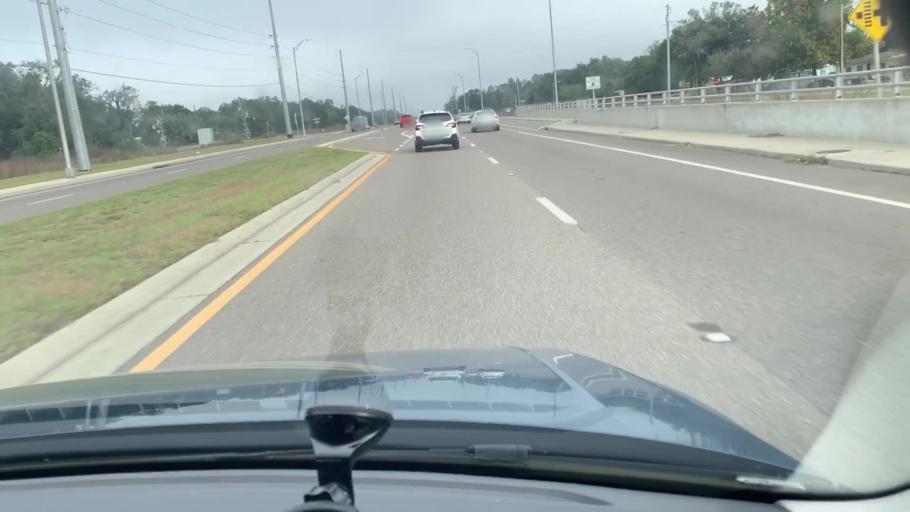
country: US
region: Florida
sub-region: Polk County
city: Kathleen
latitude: 28.1043
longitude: -82.0125
